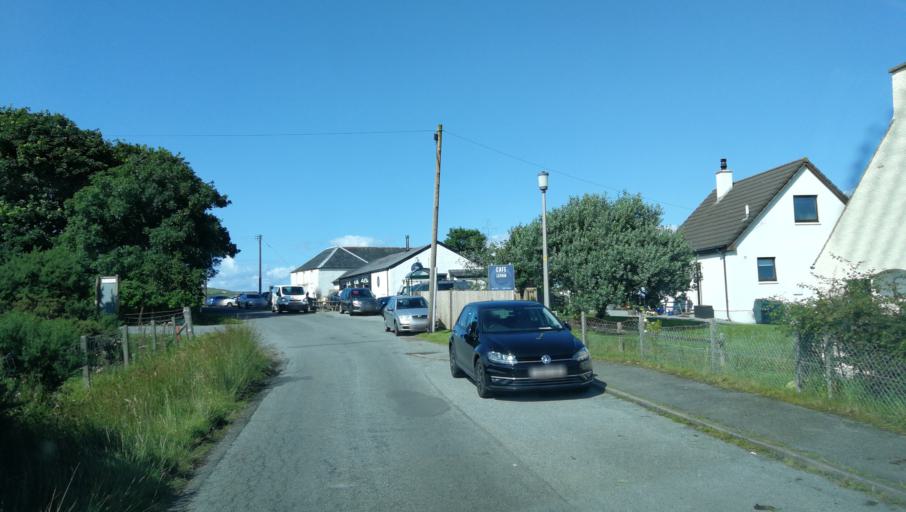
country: GB
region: Scotland
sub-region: Eilean Siar
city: Harris
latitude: 57.4484
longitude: -6.7074
